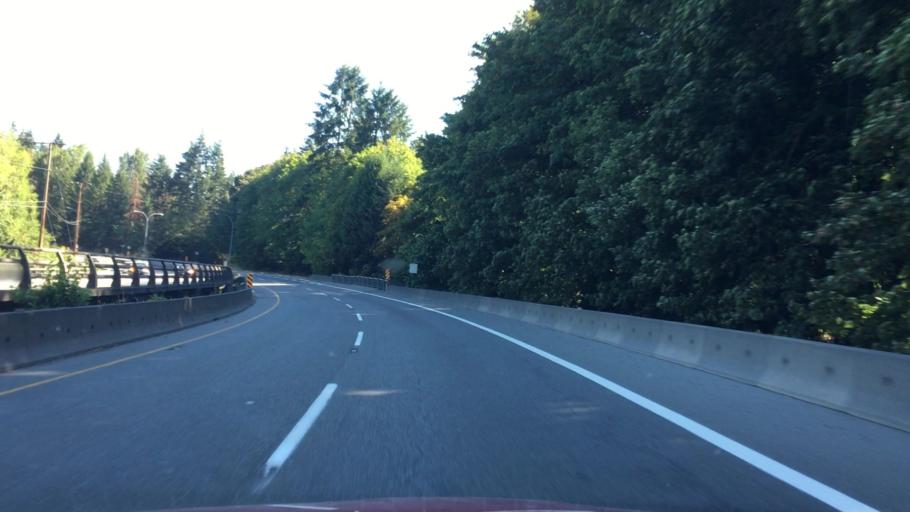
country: CA
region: British Columbia
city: North Cowichan
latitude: 48.8509
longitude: -123.7232
